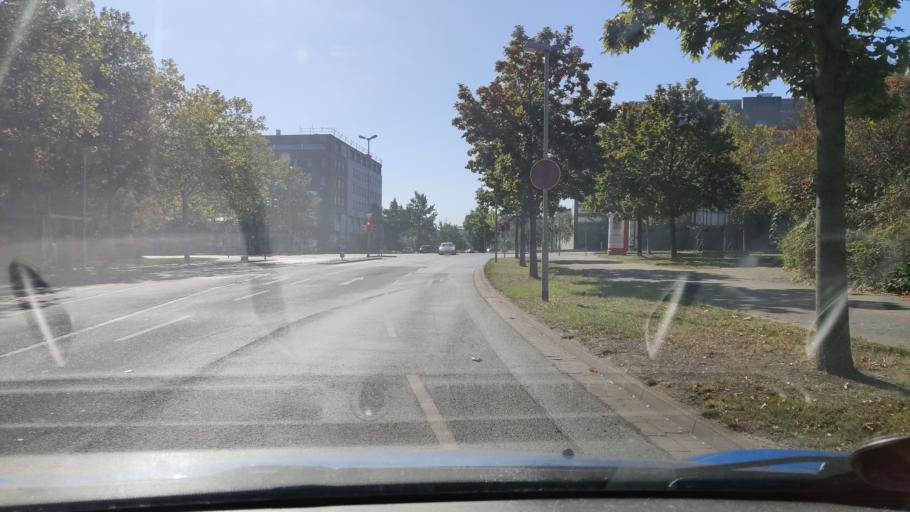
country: DE
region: Lower Saxony
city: Hannover
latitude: 52.3929
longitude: 9.7982
